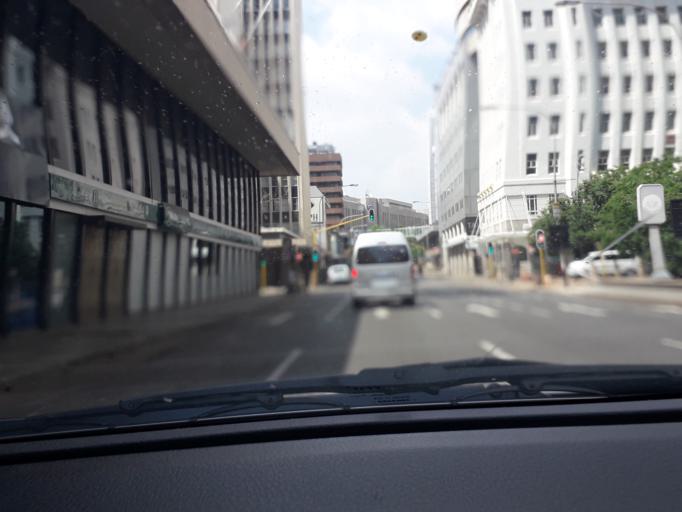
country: ZA
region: Gauteng
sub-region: City of Johannesburg Metropolitan Municipality
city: Johannesburg
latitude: -26.2064
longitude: 28.0399
